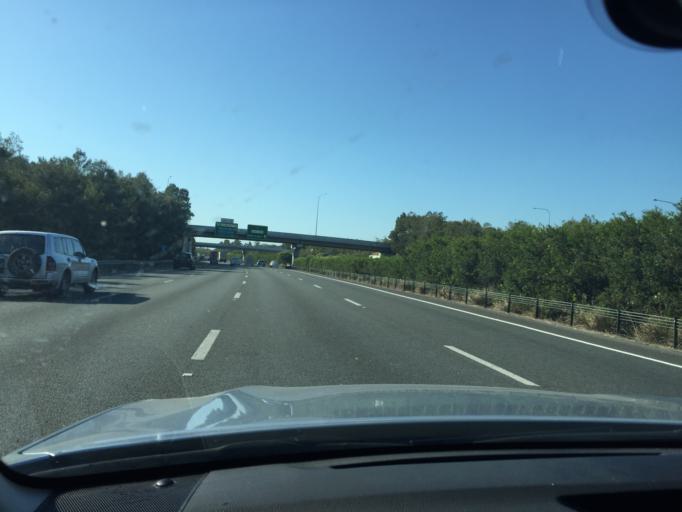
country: AU
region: Queensland
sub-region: Gold Coast
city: Yatala
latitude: -27.7183
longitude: 153.2117
